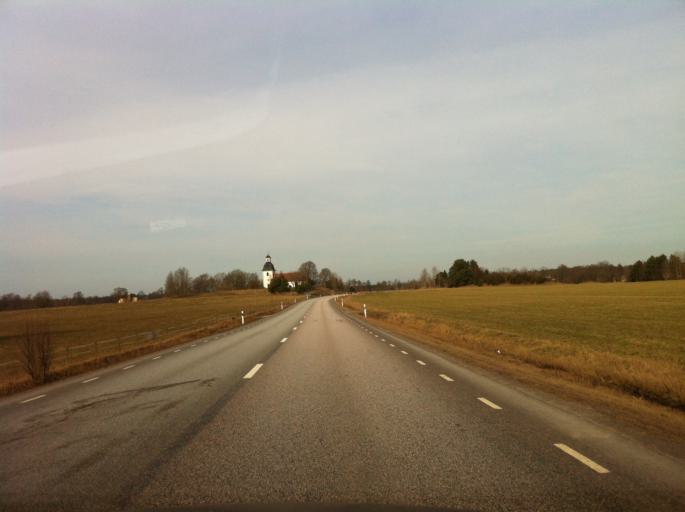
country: SE
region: Vaestra Goetaland
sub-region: Mariestads Kommun
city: Mariestad
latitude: 58.7897
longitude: 13.9657
